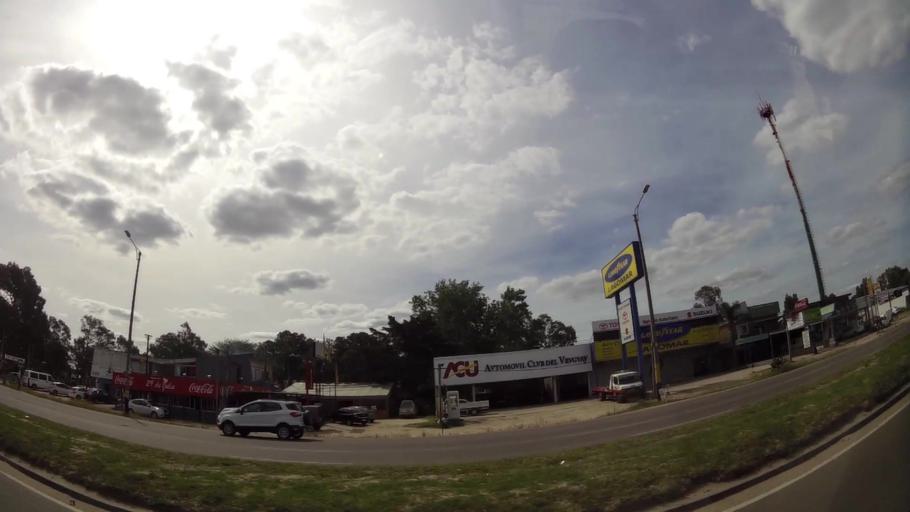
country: UY
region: Canelones
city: Barra de Carrasco
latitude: -34.8348
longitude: -55.9818
